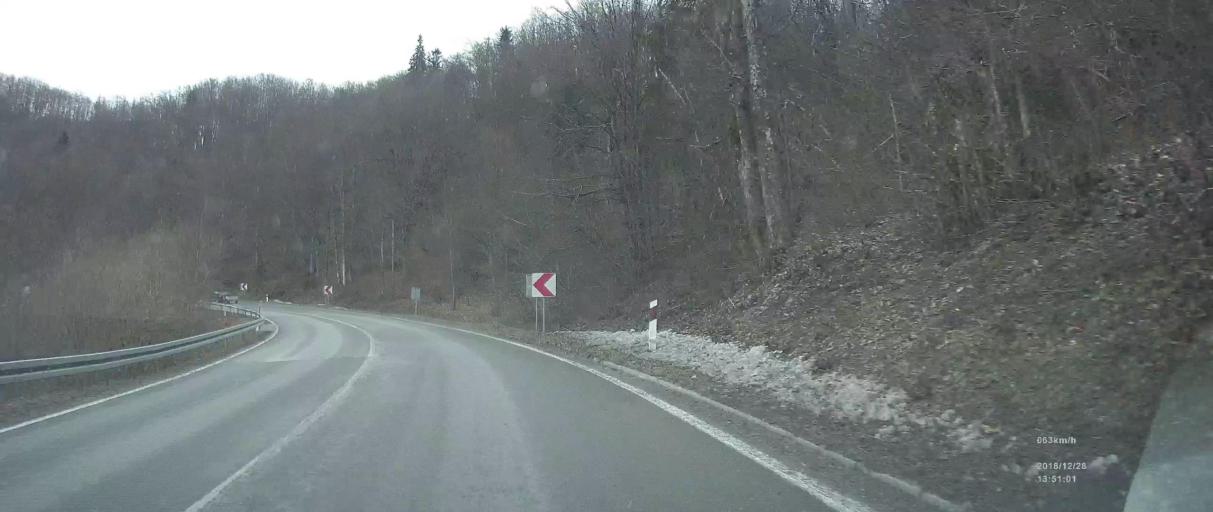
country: HR
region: Primorsko-Goranska
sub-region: Grad Delnice
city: Delnice
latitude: 45.3924
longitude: 14.8355
